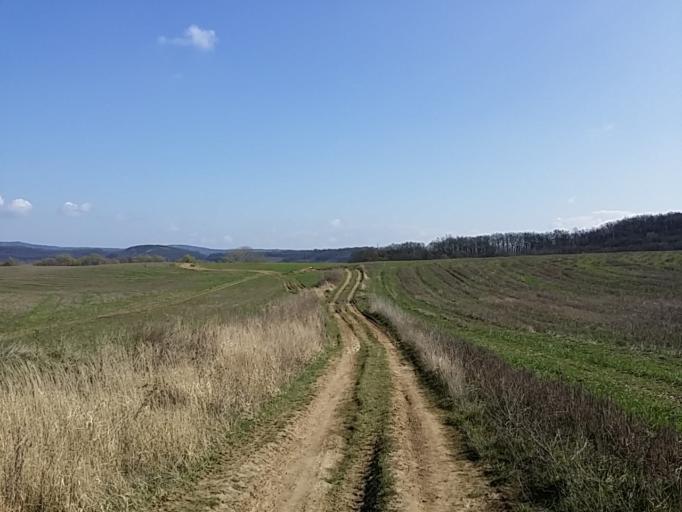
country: HU
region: Fejer
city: Szarliget
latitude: 47.5165
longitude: 18.4803
